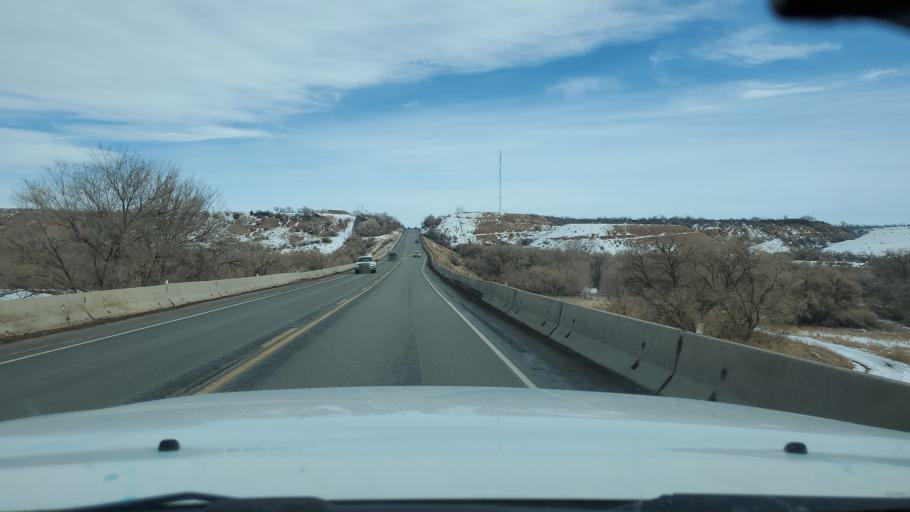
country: US
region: Utah
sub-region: Duchesne County
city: Roosevelt
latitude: 40.3020
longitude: -109.9119
